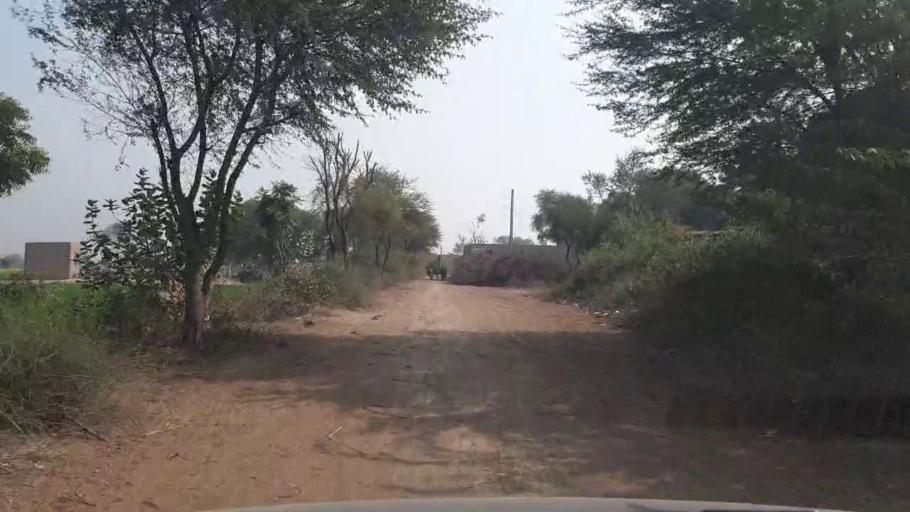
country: PK
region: Sindh
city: Hala
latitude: 25.7621
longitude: 68.4325
